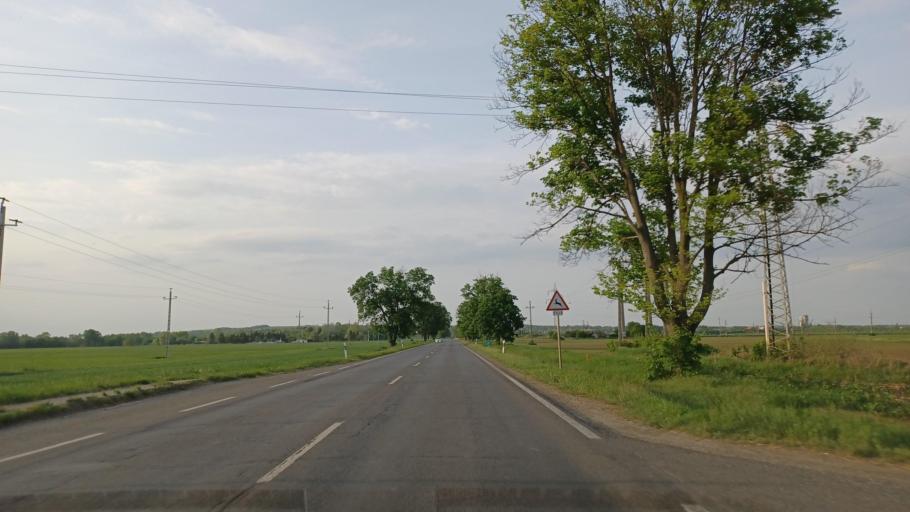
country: HU
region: Baranya
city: Lanycsok
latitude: 46.0079
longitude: 18.6547
